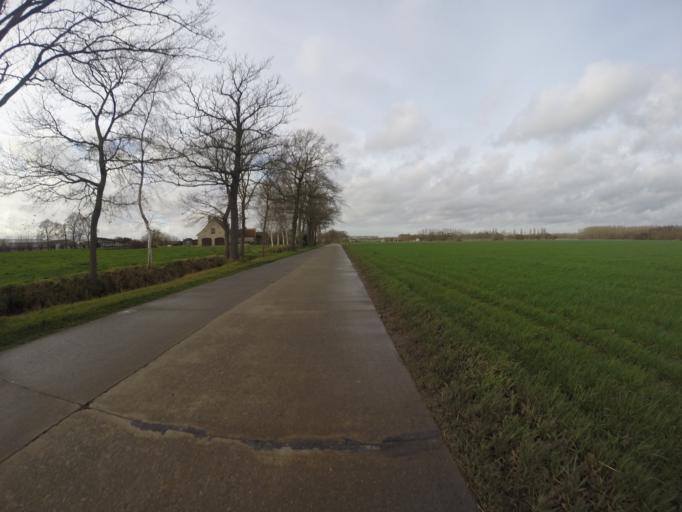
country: BE
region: Flanders
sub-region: Provincie Oost-Vlaanderen
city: Knesselare
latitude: 51.1568
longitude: 3.4233
